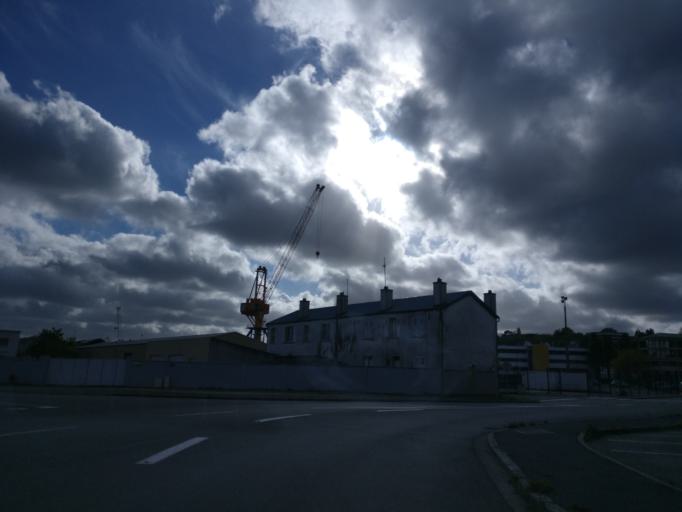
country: FR
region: Brittany
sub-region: Departement du Finistere
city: Brest
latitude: 48.3851
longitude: -4.4738
